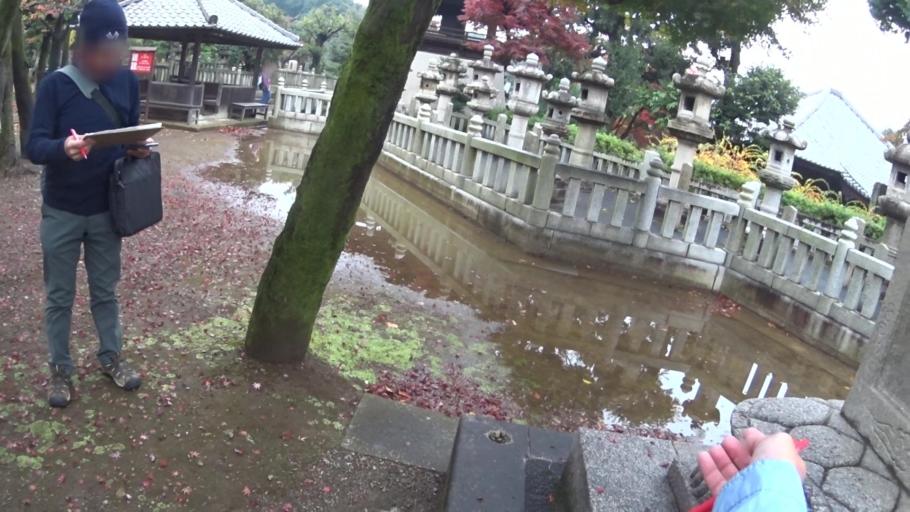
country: JP
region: Tokyo
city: Tokyo
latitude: 35.7214
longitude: 139.7262
